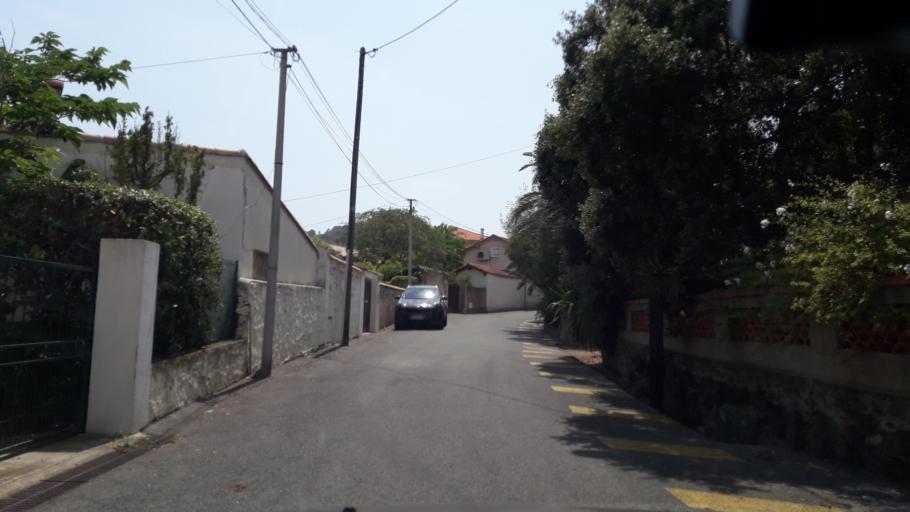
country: FR
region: Provence-Alpes-Cote d'Azur
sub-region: Departement du Var
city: Saint-Raphael
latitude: 43.4223
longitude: 6.8561
